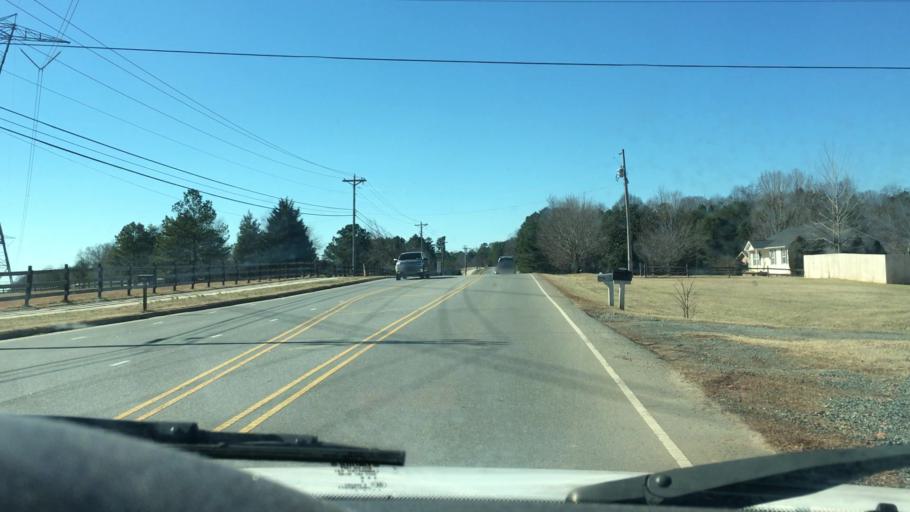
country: US
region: North Carolina
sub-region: Gaston County
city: Davidson
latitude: 35.4696
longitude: -80.8305
